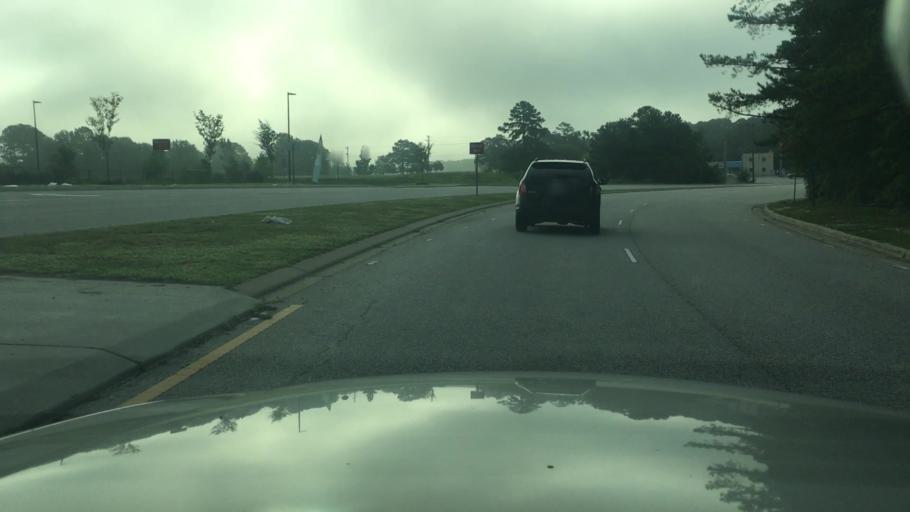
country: US
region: North Carolina
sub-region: Cumberland County
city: Hope Mills
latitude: 35.0011
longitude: -78.9019
